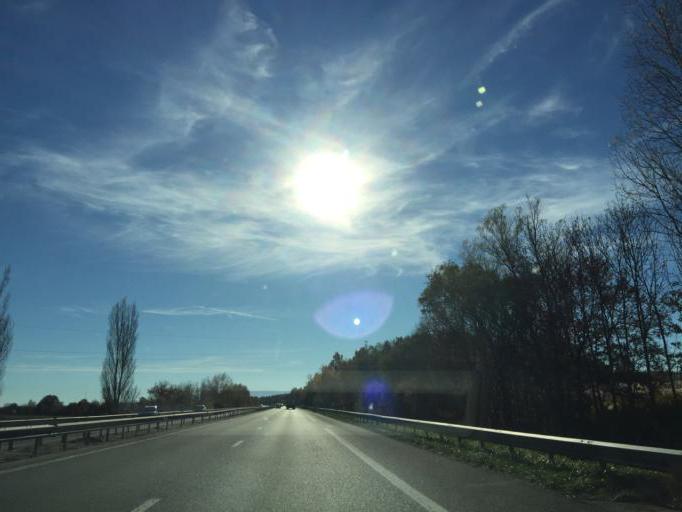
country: FR
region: Rhone-Alpes
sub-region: Departement de la Loire
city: Feurs
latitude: 45.7070
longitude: 4.1655
